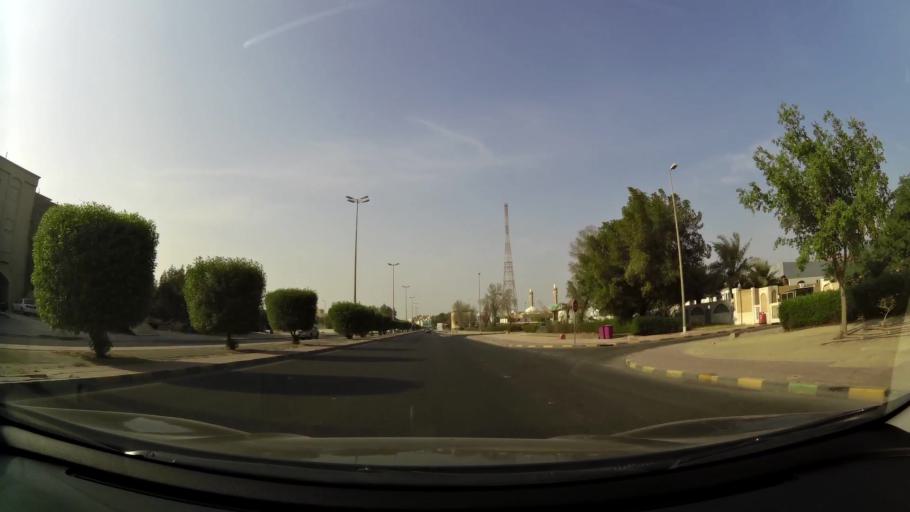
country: KW
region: Mubarak al Kabir
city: Mubarak al Kabir
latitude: 29.1696
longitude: 48.0790
